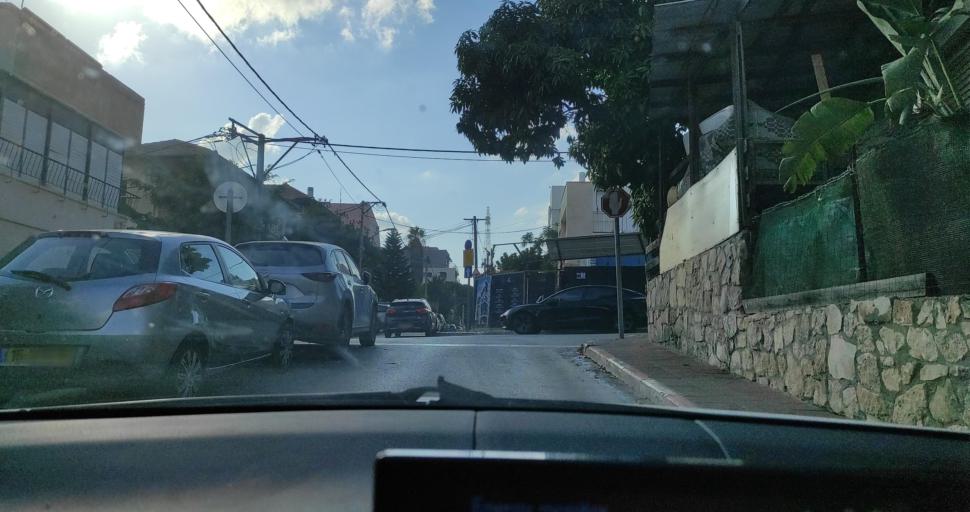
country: IL
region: Tel Aviv
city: Giv`atayim
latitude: 32.0720
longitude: 34.8209
